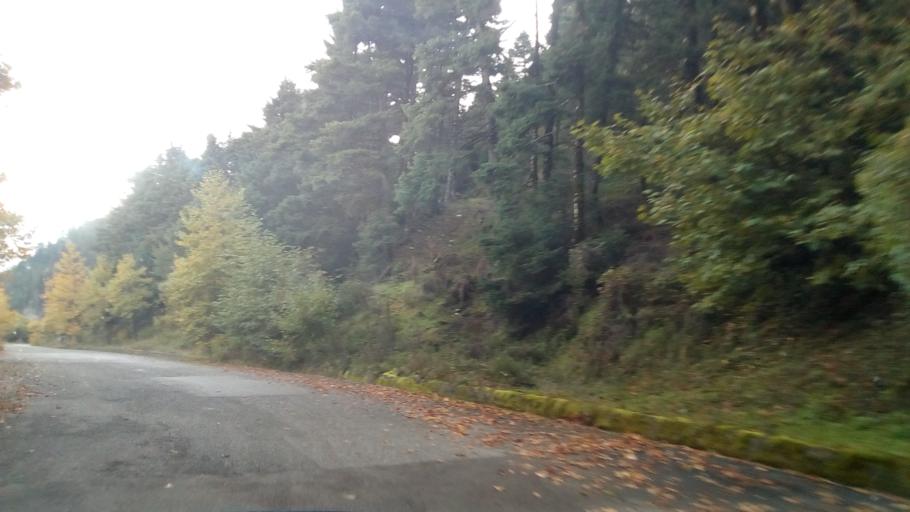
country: GR
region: West Greece
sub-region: Nomos Aitolias kai Akarnanias
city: Thermo
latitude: 38.6451
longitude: 21.8507
